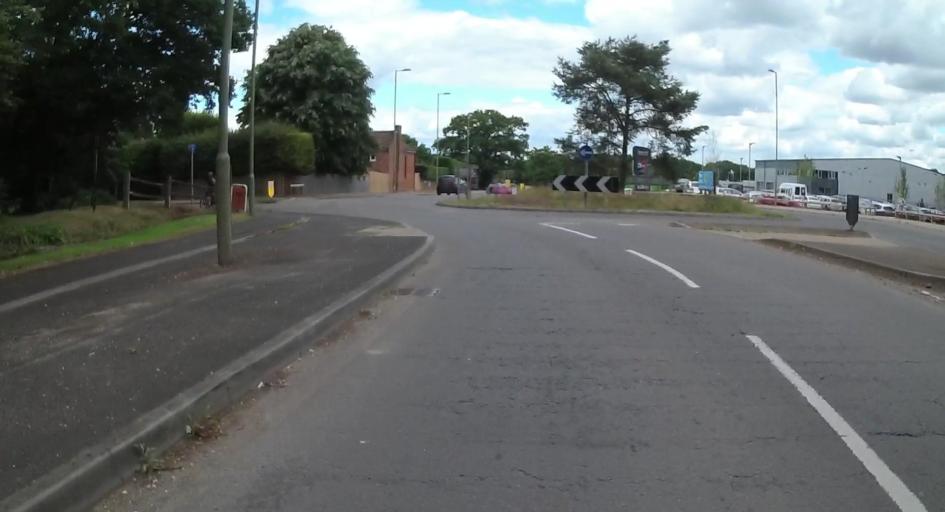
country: GB
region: England
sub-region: Hampshire
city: Fleet
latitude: 51.2572
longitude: -0.8261
